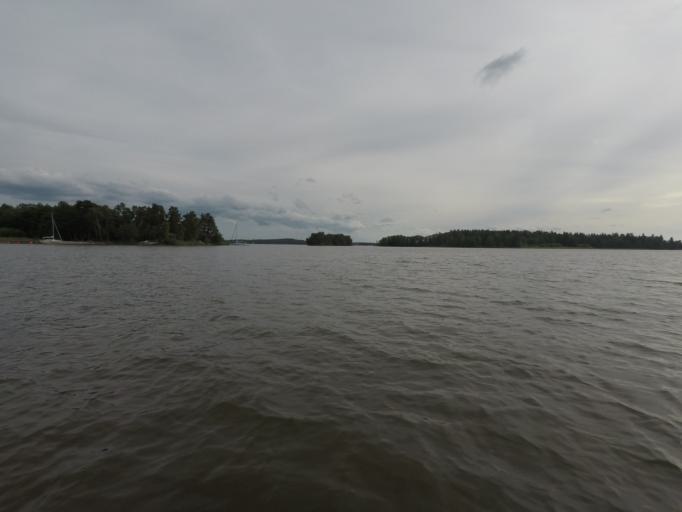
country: SE
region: Soedermanland
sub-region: Eskilstuna Kommun
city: Torshalla
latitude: 59.4780
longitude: 16.4492
